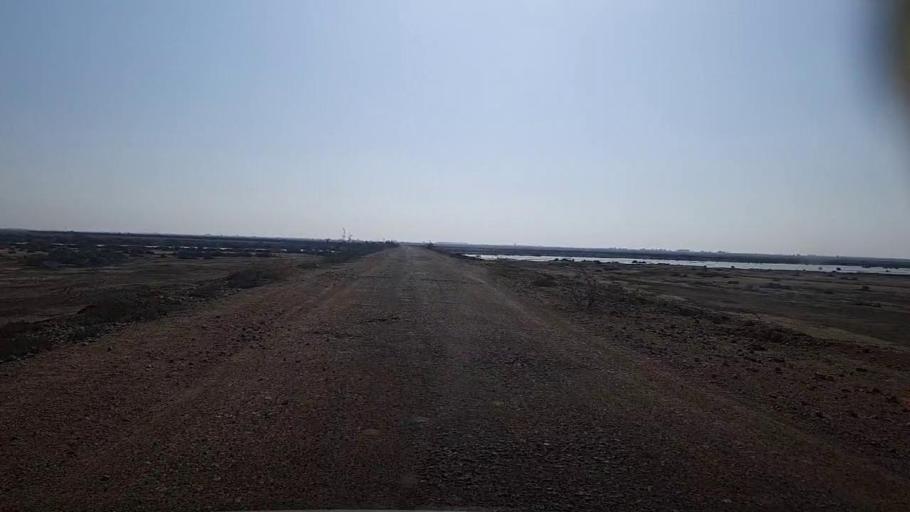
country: PK
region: Sindh
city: Mirpur Sakro
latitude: 24.5188
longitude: 67.4912
